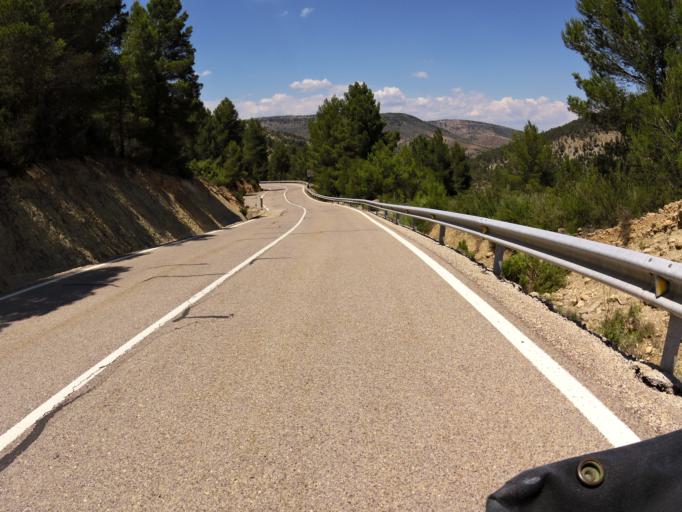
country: ES
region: Castille-La Mancha
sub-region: Provincia de Cuenca
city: Santa Cruz de Moya
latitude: 39.9807
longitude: -1.2736
